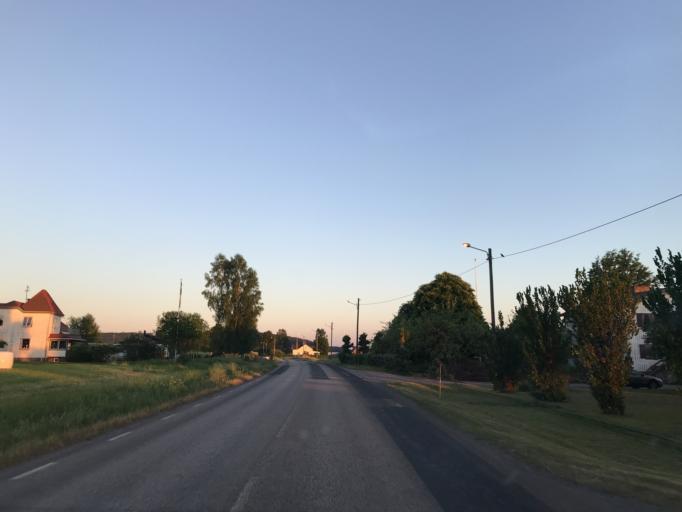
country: SE
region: Vaestra Goetaland
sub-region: Marks Kommun
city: Horred
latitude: 57.4342
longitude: 12.5164
